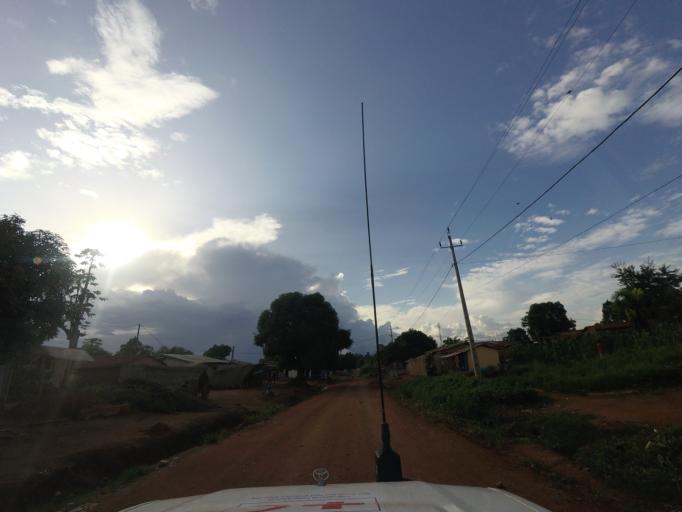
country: GN
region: Nzerekore
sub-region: Nzerekore Prefecture
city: Nzerekore
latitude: 7.7297
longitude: -8.8273
